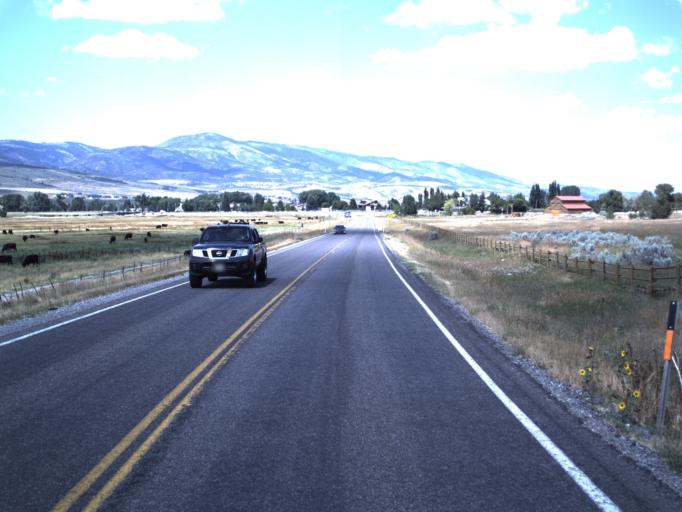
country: US
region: Utah
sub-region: Rich County
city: Randolph
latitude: 41.9011
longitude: -111.3728
